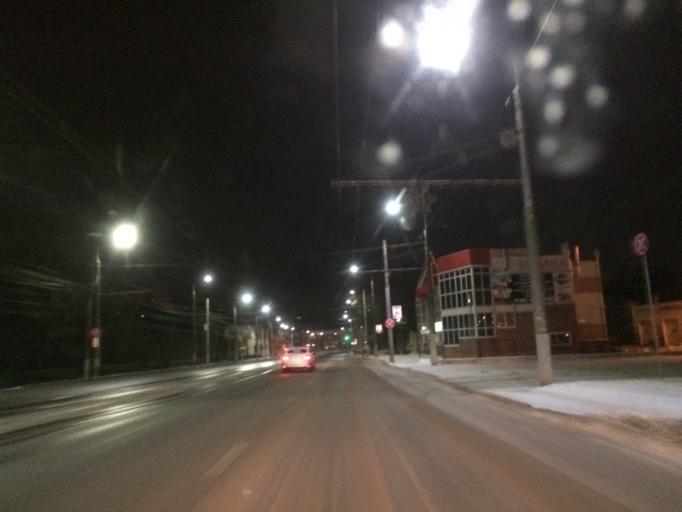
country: RU
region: Tula
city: Tula
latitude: 54.1934
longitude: 37.6298
